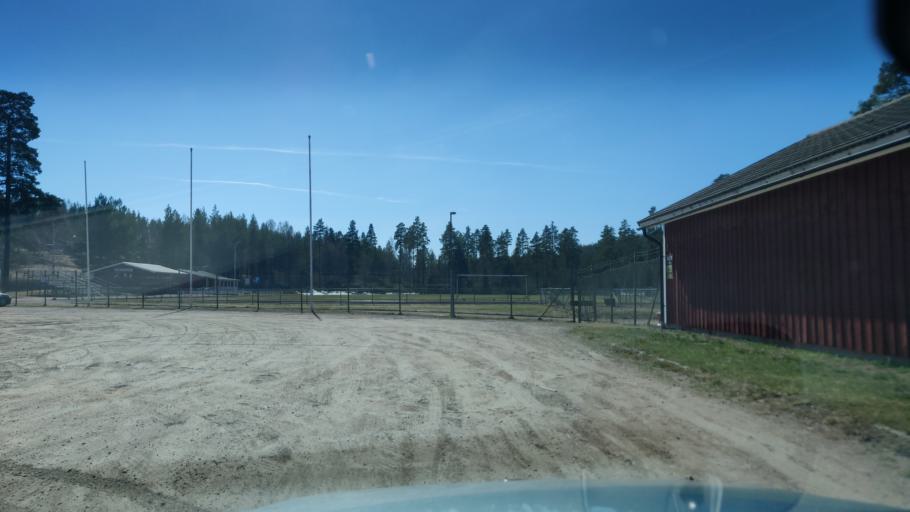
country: SE
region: Vaermland
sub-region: Hagfors Kommun
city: Ekshaerad
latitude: 60.1714
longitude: 13.4866
